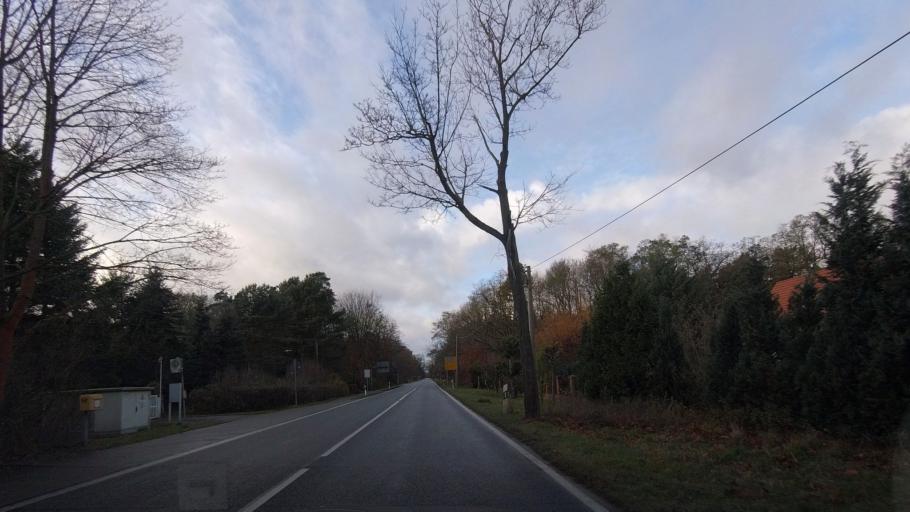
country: DE
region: Brandenburg
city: Niedergorsdorf
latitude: 52.0353
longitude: 12.9441
